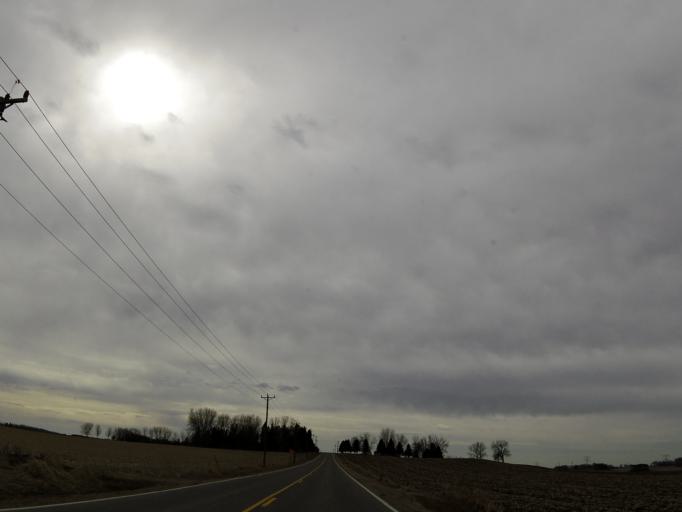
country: US
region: Minnesota
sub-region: Washington County
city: Afton
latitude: 44.8801
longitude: -92.8428
